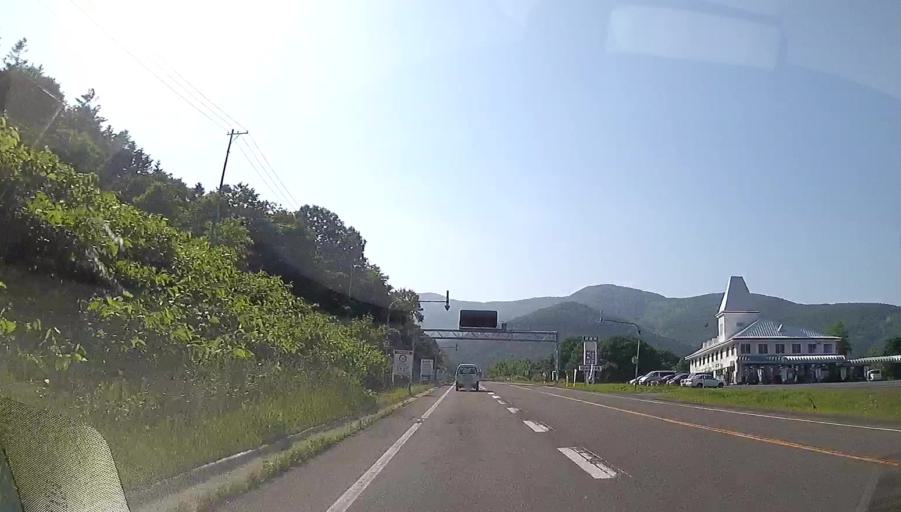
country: JP
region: Hokkaido
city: Otofuke
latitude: 42.9735
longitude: 142.8065
